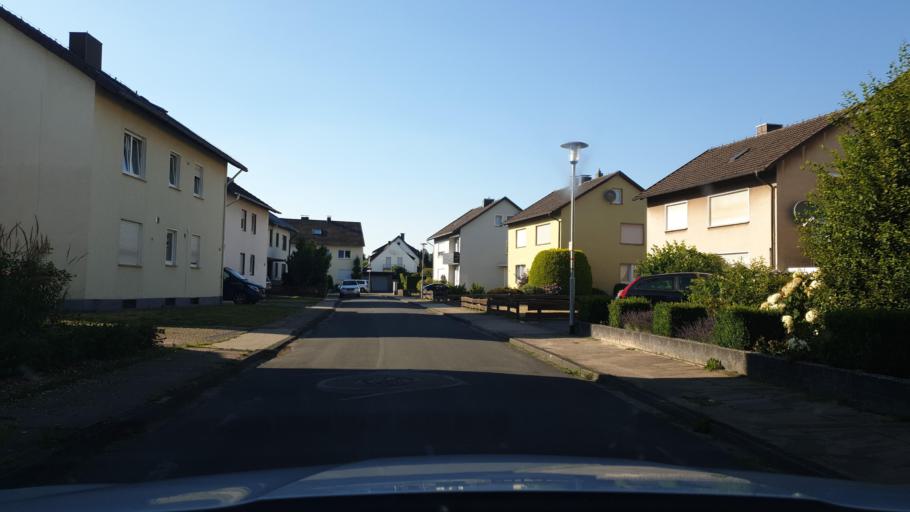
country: DE
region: North Rhine-Westphalia
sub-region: Regierungsbezirk Detmold
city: Bad Salzuflen
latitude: 52.0695
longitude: 8.7685
